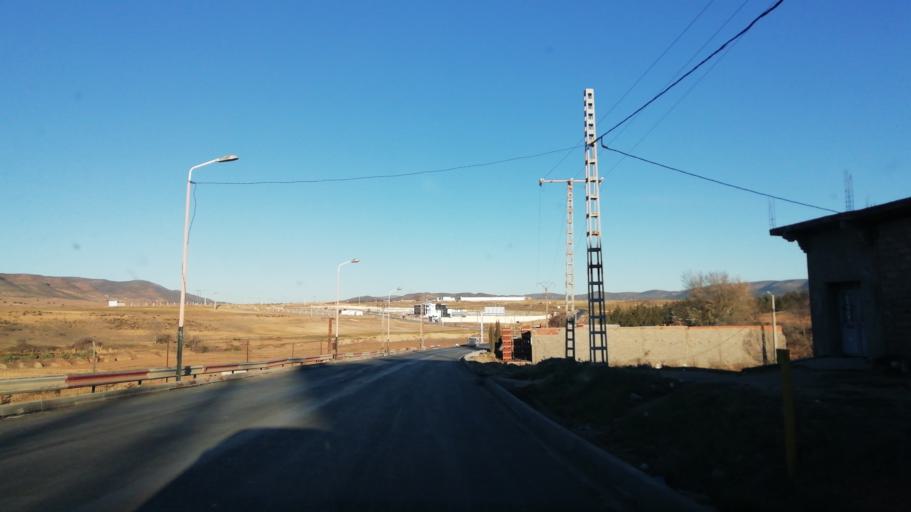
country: DZ
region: Tlemcen
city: Sebdou
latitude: 34.6548
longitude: -1.3140
